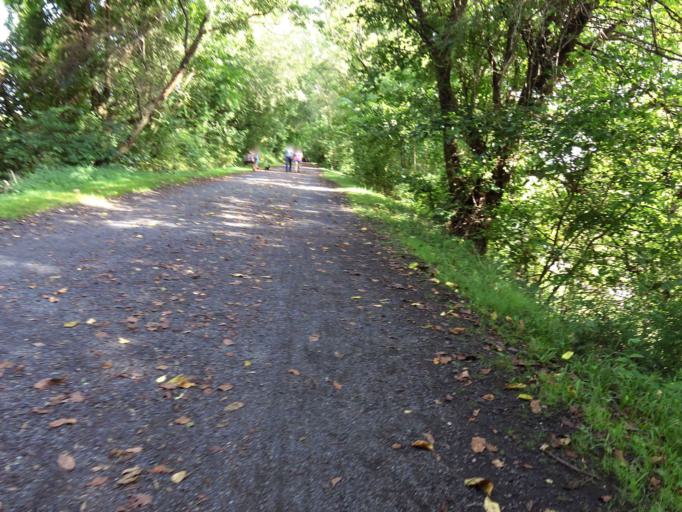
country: US
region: Virginia
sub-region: Washington County
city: Abingdon
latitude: 36.7064
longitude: -81.9666
